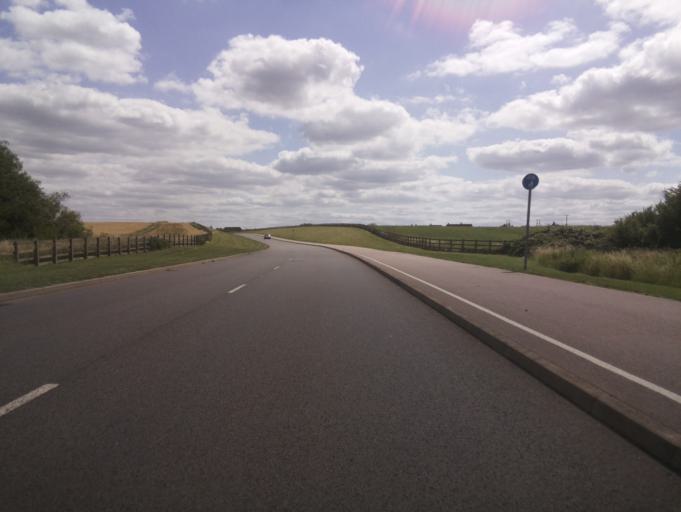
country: GB
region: England
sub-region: Buckinghamshire
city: Aylesbury
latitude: 51.8373
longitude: -0.8287
